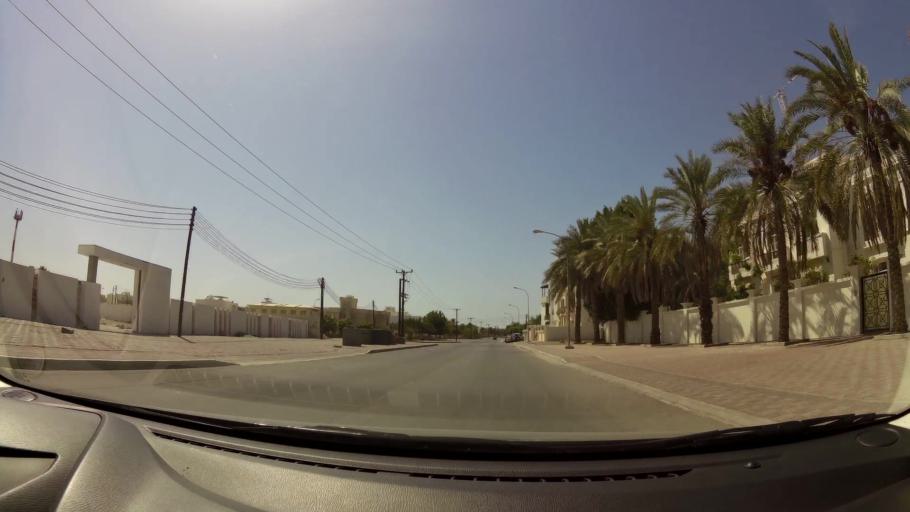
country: OM
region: Muhafazat Masqat
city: As Sib al Jadidah
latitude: 23.6325
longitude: 58.2206
